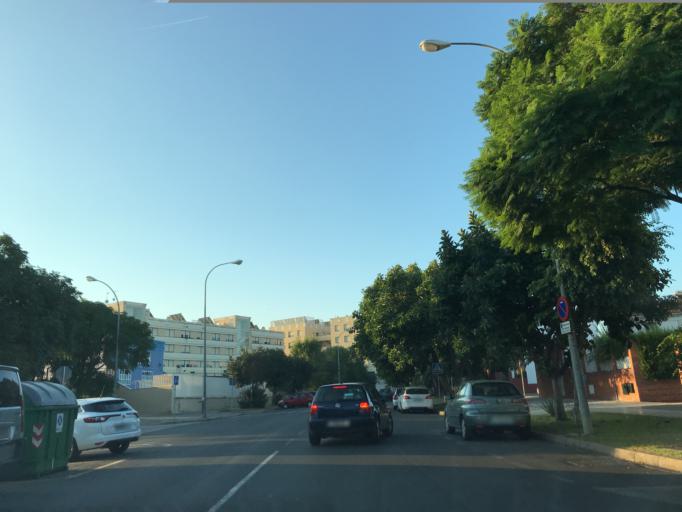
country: ES
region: Andalusia
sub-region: Provincia de Sevilla
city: Sevilla
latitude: 37.4107
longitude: -5.9346
